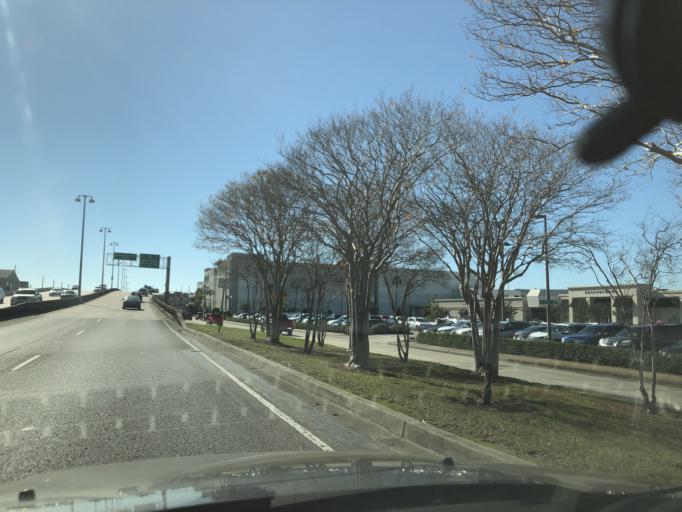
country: US
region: Louisiana
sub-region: Jefferson Parish
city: Metairie
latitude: 30.0067
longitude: -90.1553
